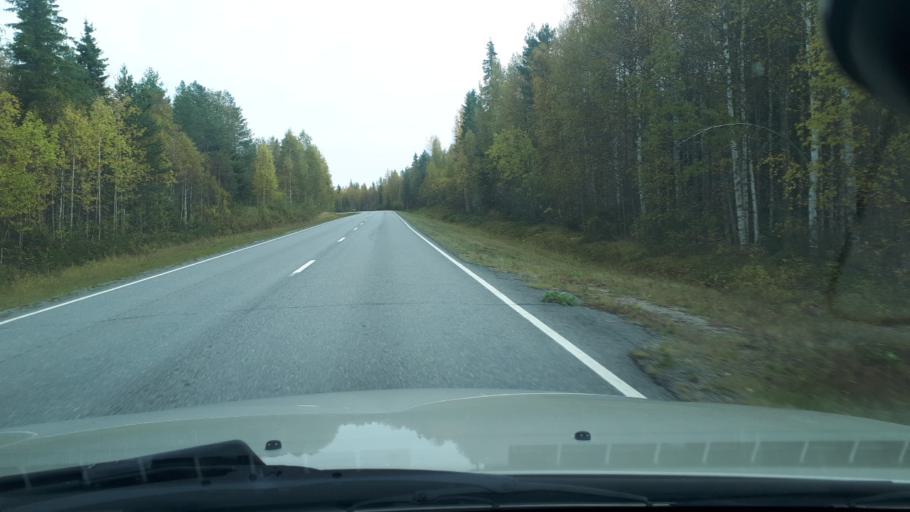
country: FI
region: Lapland
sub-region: Rovaniemi
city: Ranua
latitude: 66.0035
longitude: 26.2583
